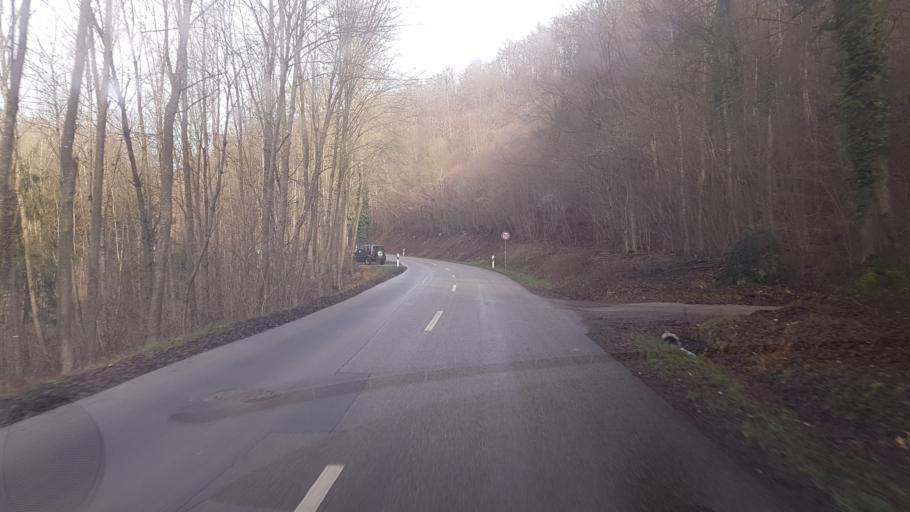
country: DE
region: Baden-Wuerttemberg
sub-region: Regierungsbezirk Stuttgart
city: Braunsbach
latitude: 49.2046
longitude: 9.8033
